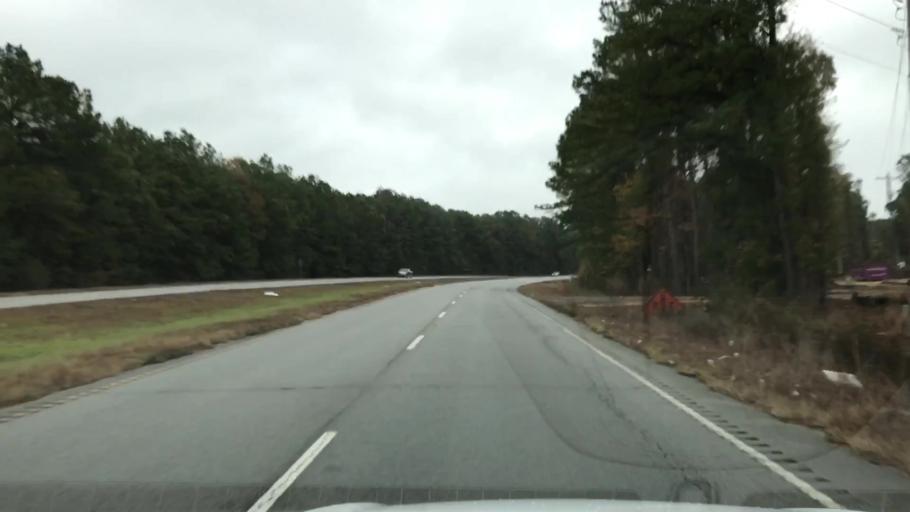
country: US
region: South Carolina
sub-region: Charleston County
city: Awendaw
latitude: 32.9435
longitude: -79.7056
